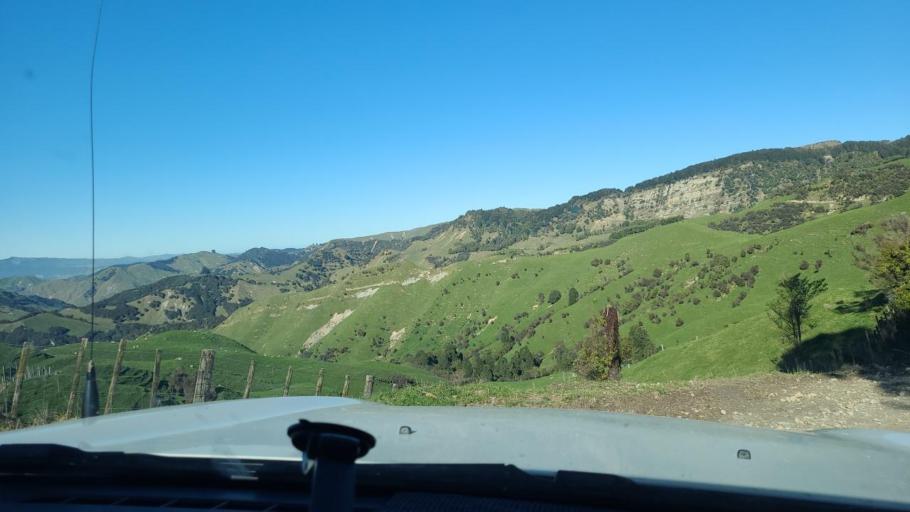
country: NZ
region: Hawke's Bay
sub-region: Wairoa District
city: Wairoa
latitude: -38.6810
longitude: 177.4675
